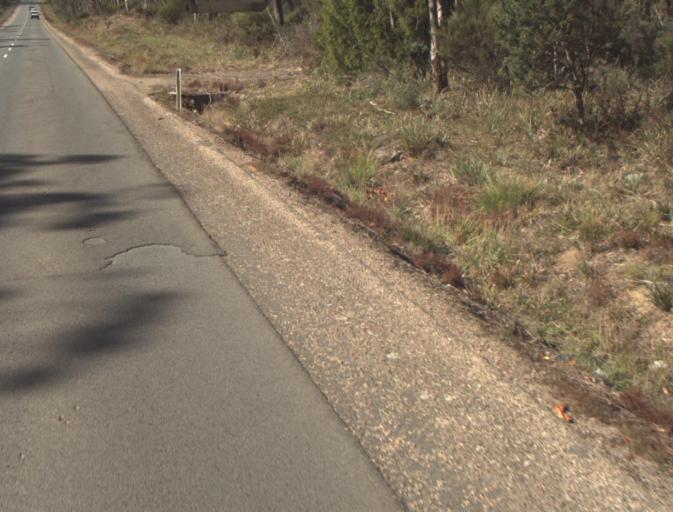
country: AU
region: Tasmania
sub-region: Launceston
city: Mayfield
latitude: -41.3175
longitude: 147.1922
